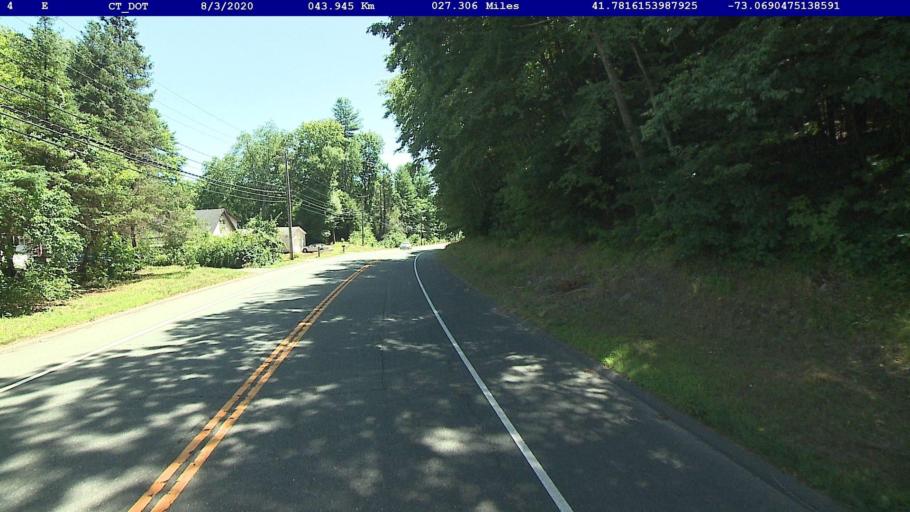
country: US
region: Connecticut
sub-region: Litchfield County
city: Northwest Harwinton
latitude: 41.7816
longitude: -73.0690
